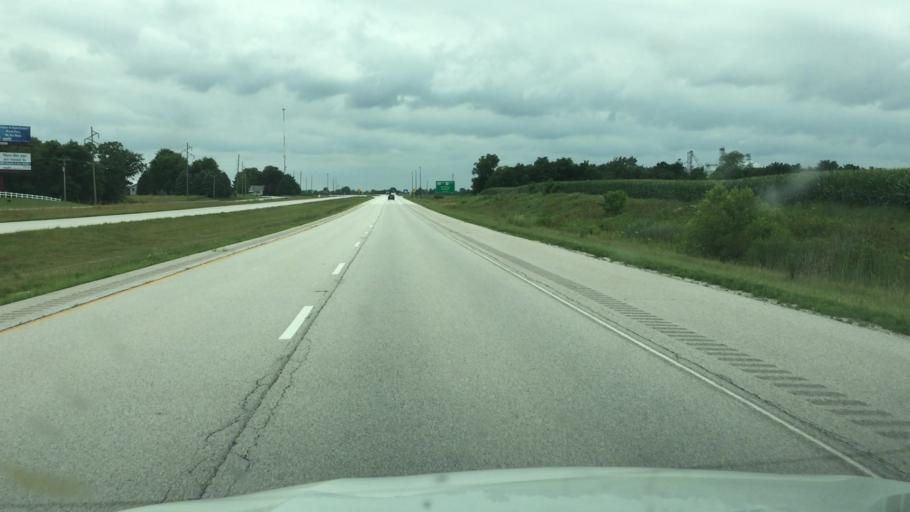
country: US
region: Illinois
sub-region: Hancock County
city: Carthage
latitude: 40.4161
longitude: -91.0951
